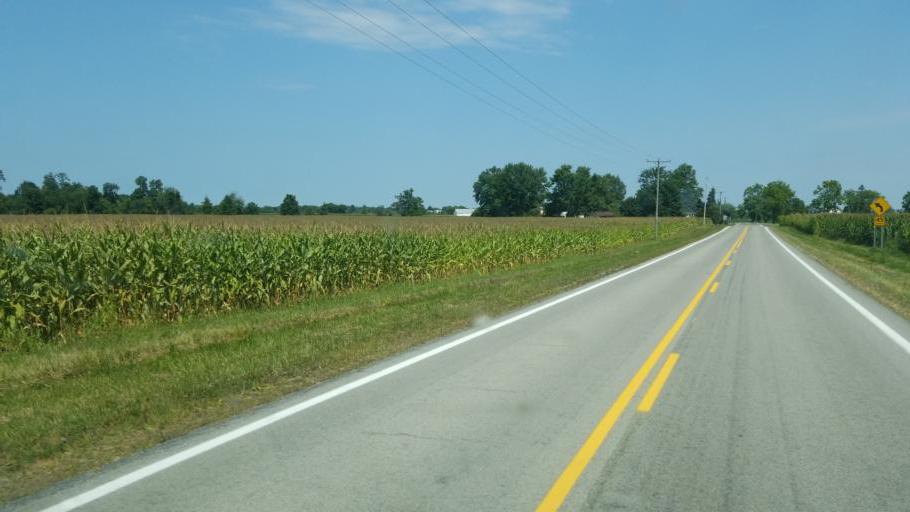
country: US
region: Ohio
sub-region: Marion County
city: Marion
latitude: 40.7157
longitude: -83.1279
